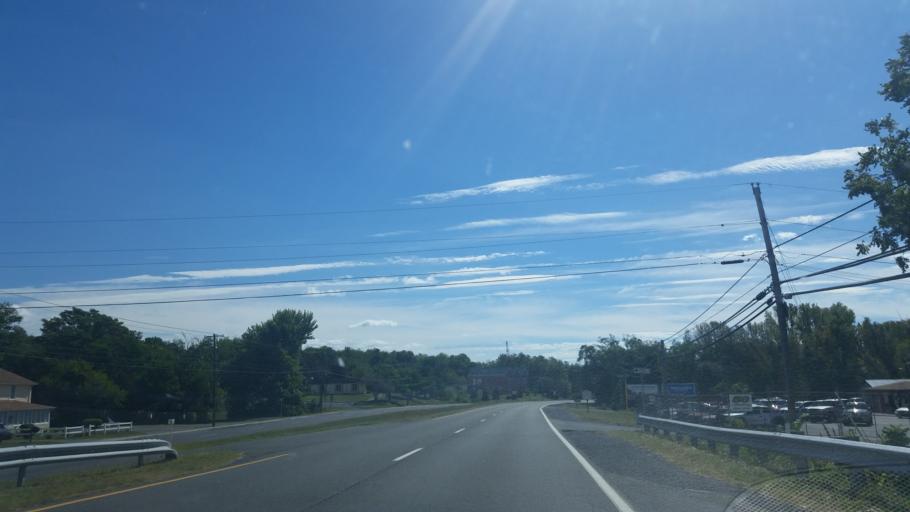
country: US
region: Virginia
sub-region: City of Winchester
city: Winchester
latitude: 39.2063
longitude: -78.1694
